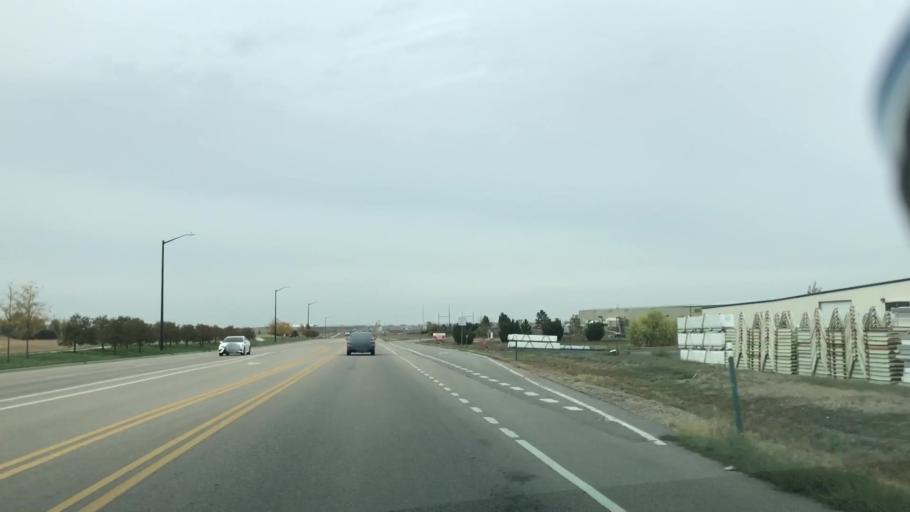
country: US
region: Colorado
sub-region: Larimer County
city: Loveland
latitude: 40.4400
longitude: -105.0204
